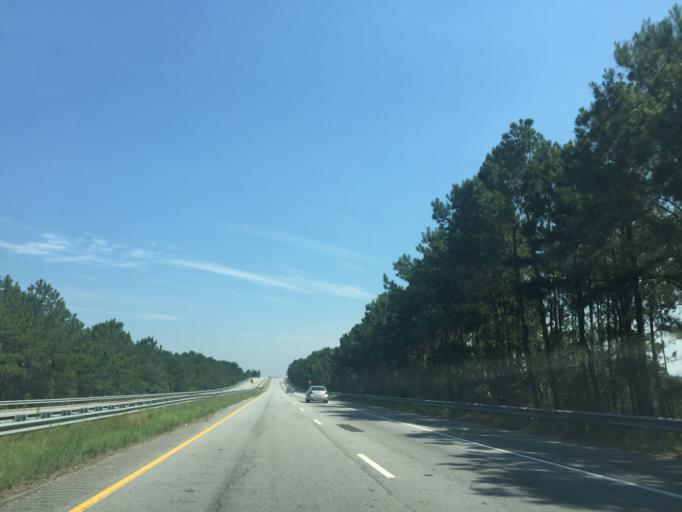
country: US
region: Georgia
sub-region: Chatham County
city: Georgetown
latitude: 31.9936
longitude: -81.1998
